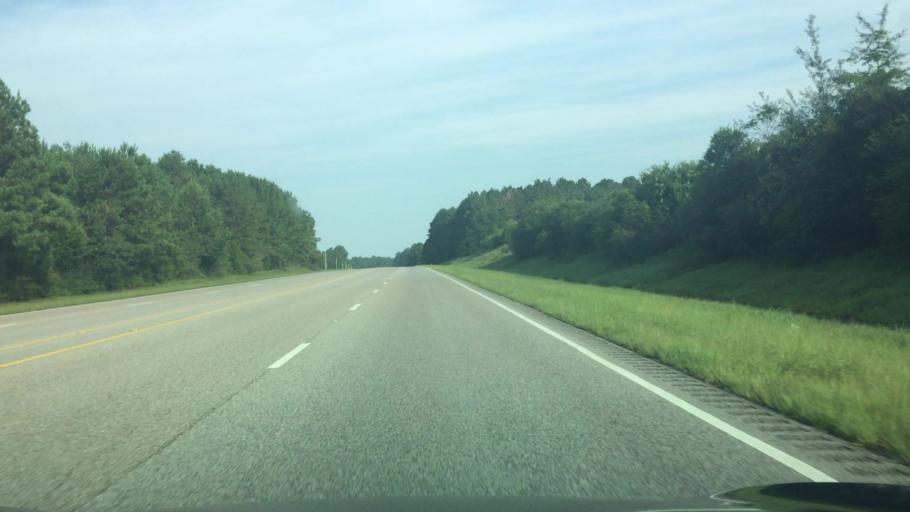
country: US
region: Alabama
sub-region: Covington County
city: Andalusia
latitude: 31.4018
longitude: -86.5877
